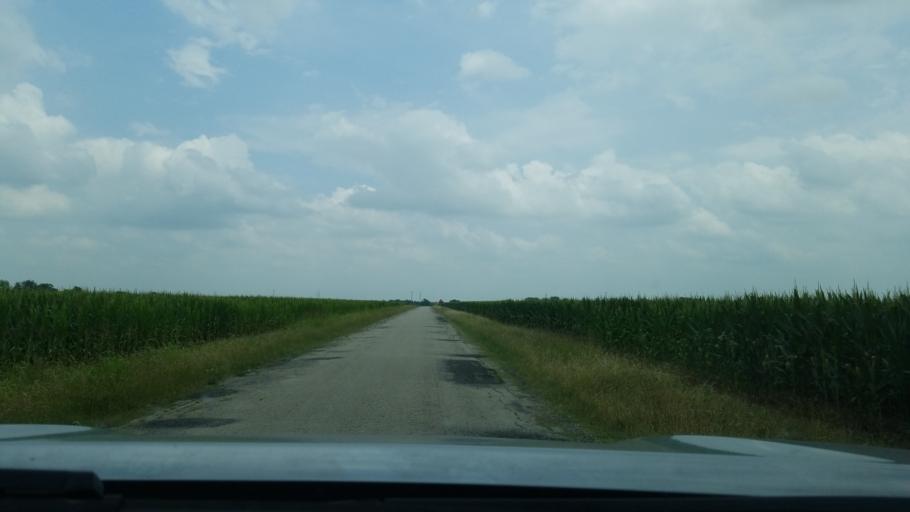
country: US
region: Texas
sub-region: Guadalupe County
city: Geronimo
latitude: 29.6802
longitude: -98.0075
